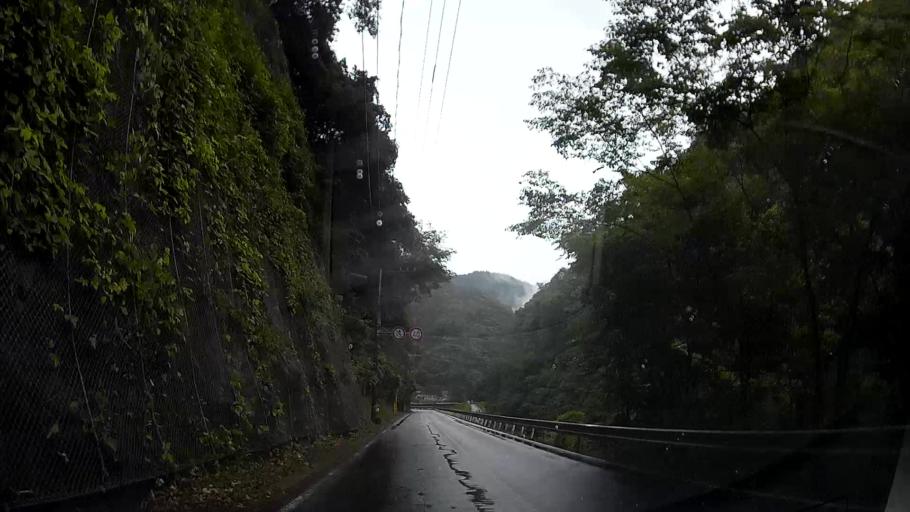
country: JP
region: Oita
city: Tsukawaki
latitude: 33.1849
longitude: 131.0256
